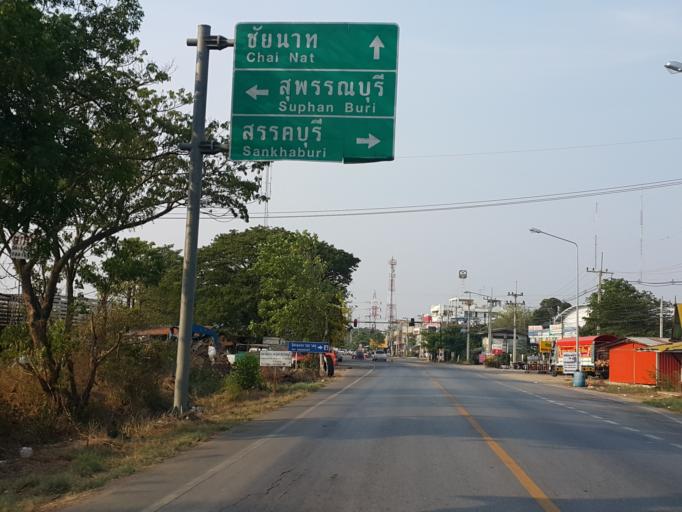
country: TH
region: Chai Nat
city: Sankhaburi
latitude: 15.0427
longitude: 100.1481
